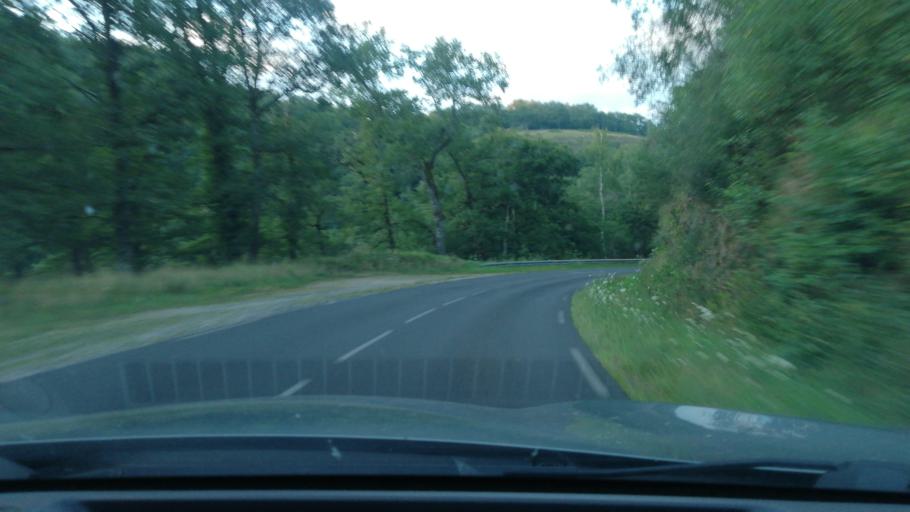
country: FR
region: Auvergne
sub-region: Departement du Cantal
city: Laroquebrou
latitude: 44.9671
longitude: 2.1811
